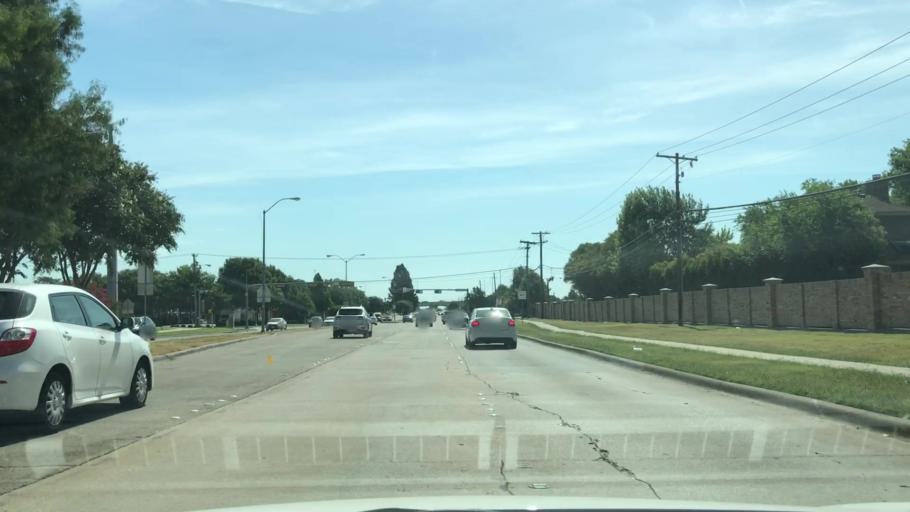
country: US
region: Texas
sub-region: Collin County
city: Plano
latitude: 33.0575
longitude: -96.7006
